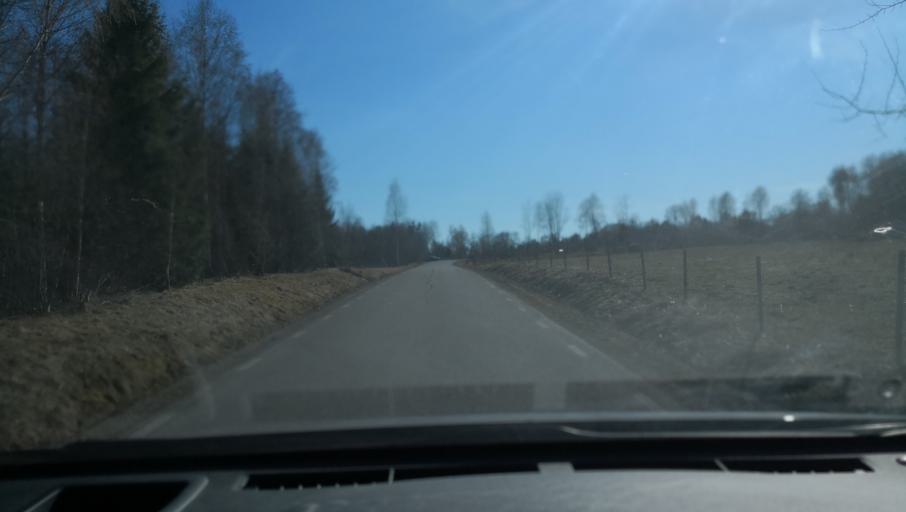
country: SE
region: Dalarna
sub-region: Avesta Kommun
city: Avesta
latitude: 60.0730
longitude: 16.3780
